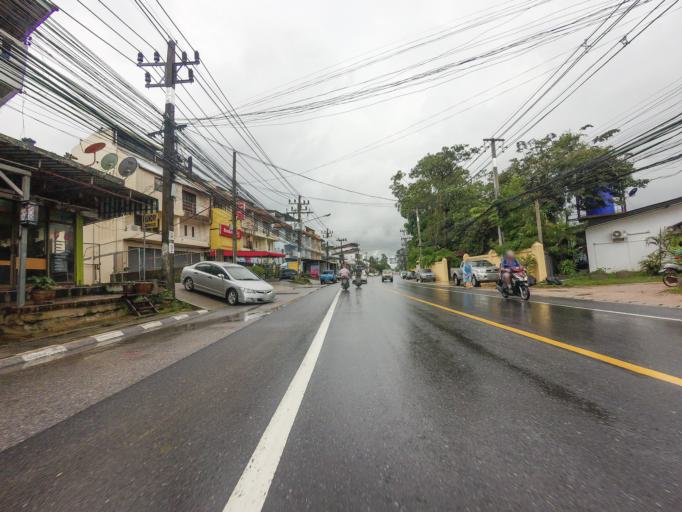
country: TH
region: Surat Thani
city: Ko Samui
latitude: 9.5120
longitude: 100.0513
